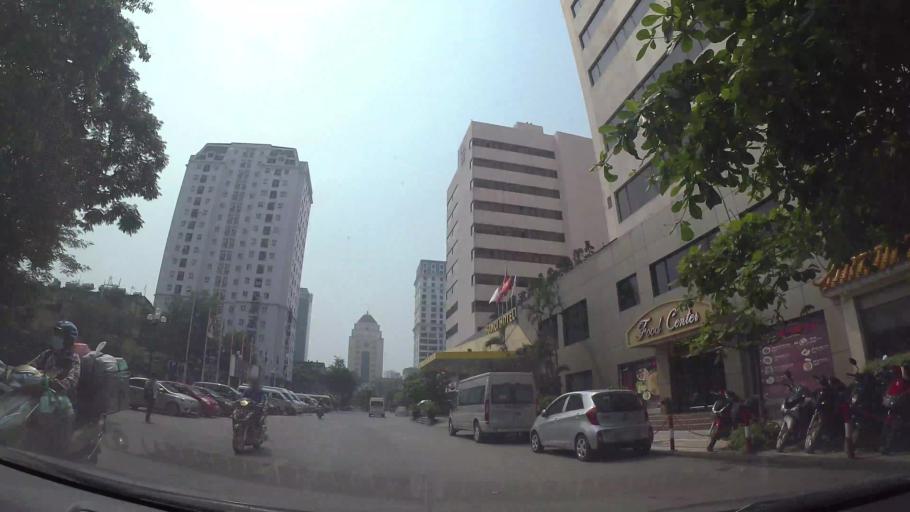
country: VN
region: Ha Noi
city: Dong Da
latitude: 21.0280
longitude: 105.8216
